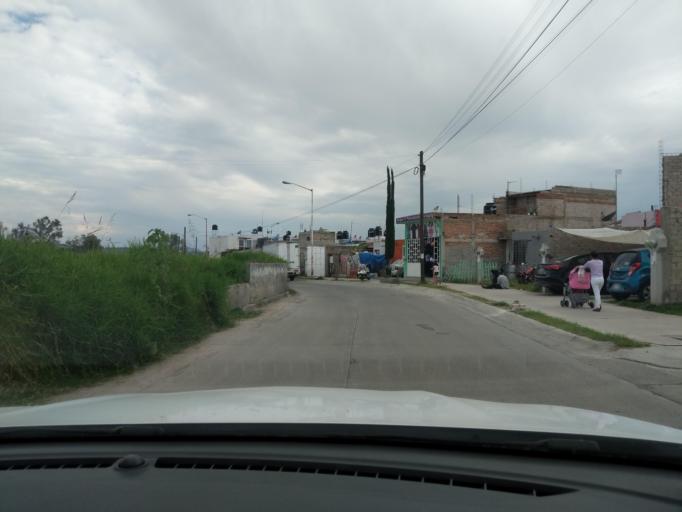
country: MX
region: Jalisco
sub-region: El Salto
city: Galaxia Bonito Jalisco
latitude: 20.5055
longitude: -103.1909
